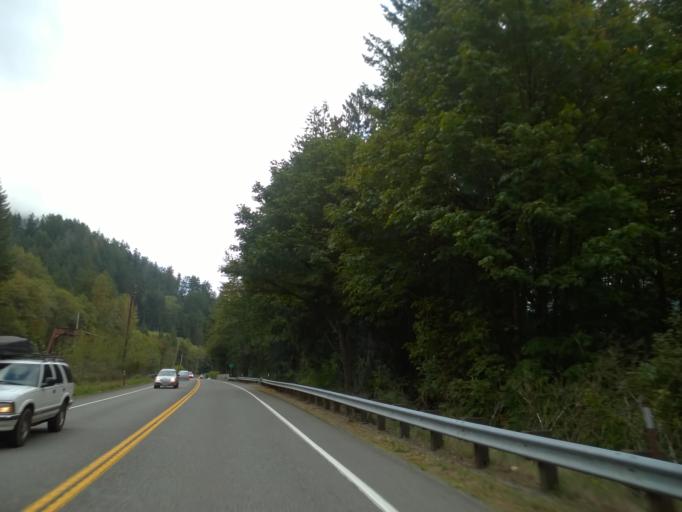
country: US
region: Washington
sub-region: Snohomish County
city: Gold Bar
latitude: 47.7868
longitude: -121.5019
